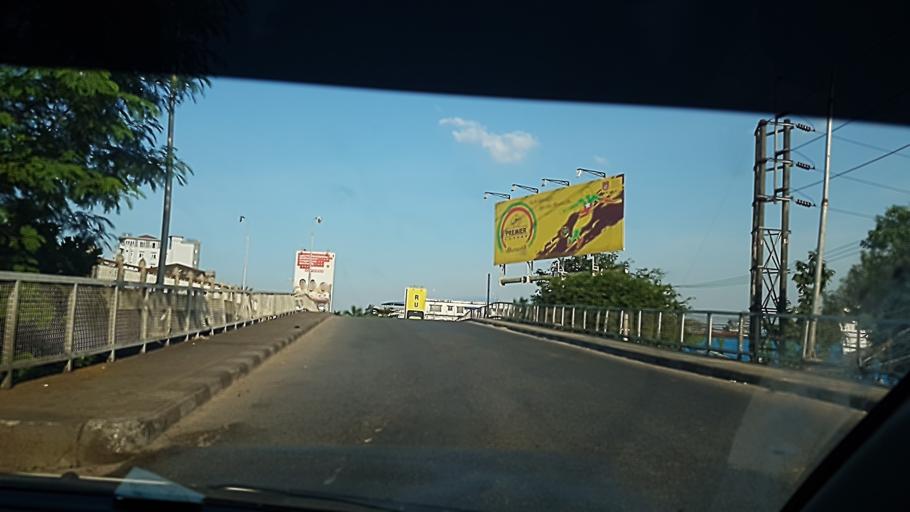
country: MM
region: Yangon
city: Yangon
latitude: 16.8198
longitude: 96.1791
